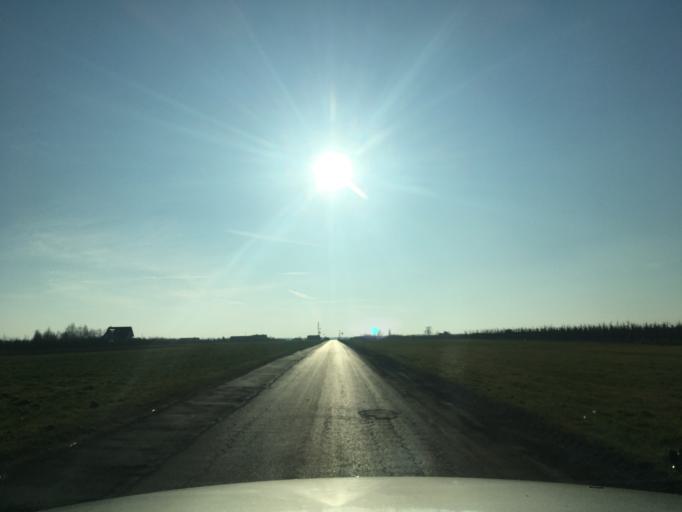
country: PL
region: Masovian Voivodeship
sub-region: Powiat pruszkowski
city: Nadarzyn
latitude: 52.0412
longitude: 20.8264
